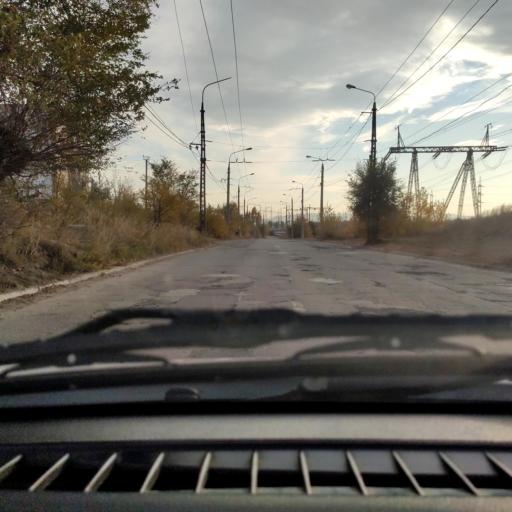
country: RU
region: Samara
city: Zhigulevsk
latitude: 53.4887
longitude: 49.5103
